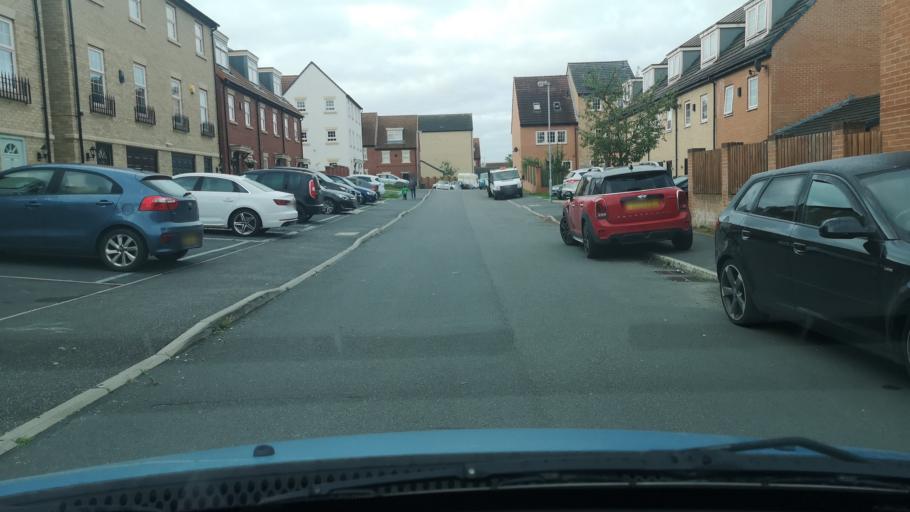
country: GB
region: England
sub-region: City and Borough of Wakefield
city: Fitzwilliam
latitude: 53.6452
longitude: -1.3543
